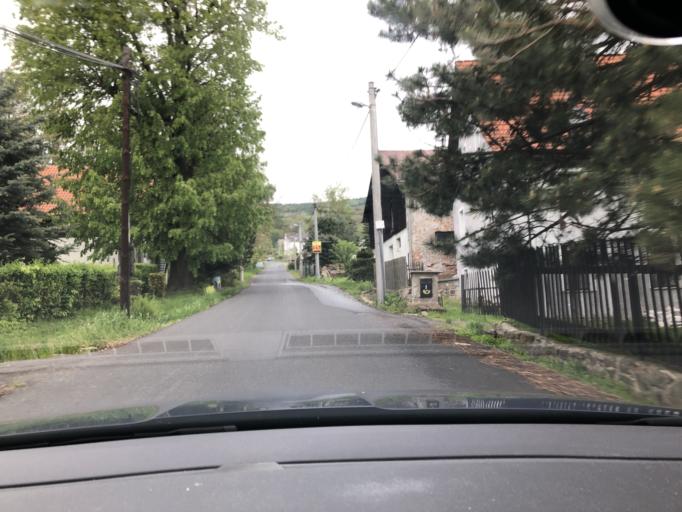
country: CZ
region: Ustecky
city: Libouchec
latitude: 50.7344
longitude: 14.0025
